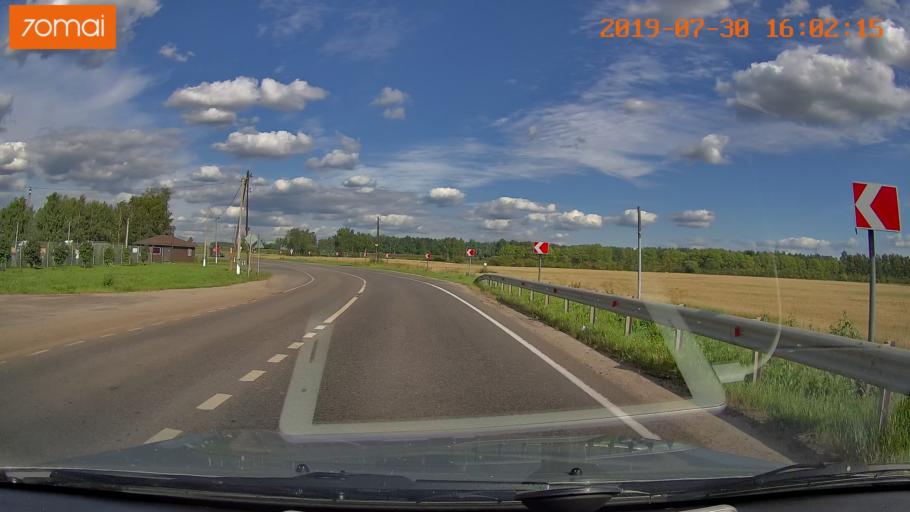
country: RU
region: Moskovskaya
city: Voskresensk
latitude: 55.2877
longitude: 38.6859
